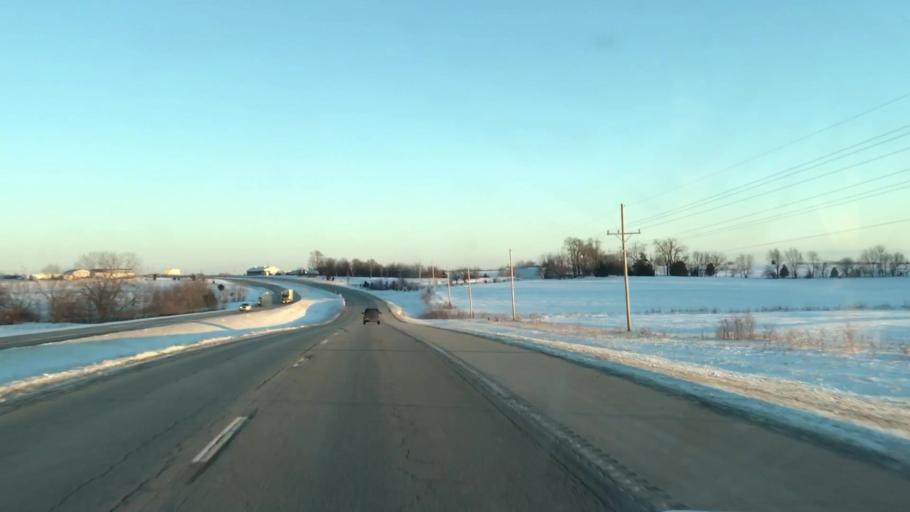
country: US
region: Missouri
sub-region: Clinton County
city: Cameron
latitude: 39.7578
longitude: -94.3451
